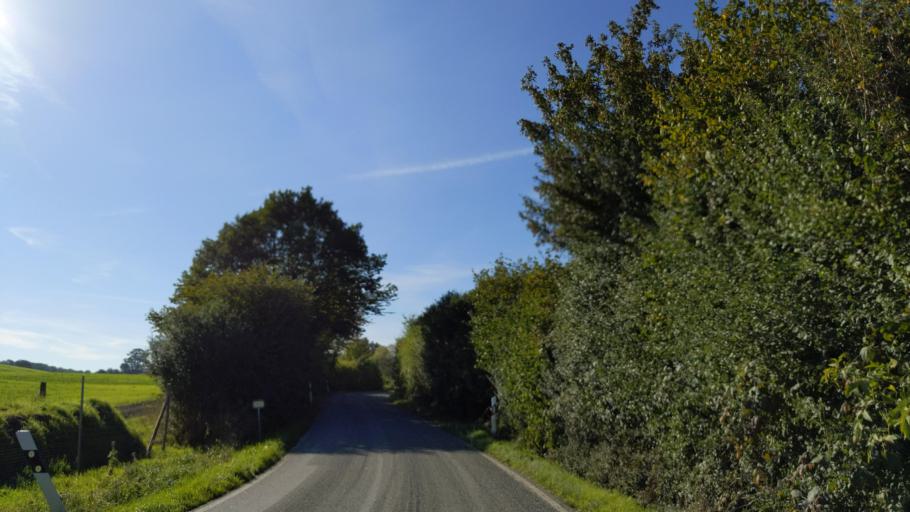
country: DE
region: Schleswig-Holstein
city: Ahrensbok
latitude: 53.9987
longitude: 10.6111
